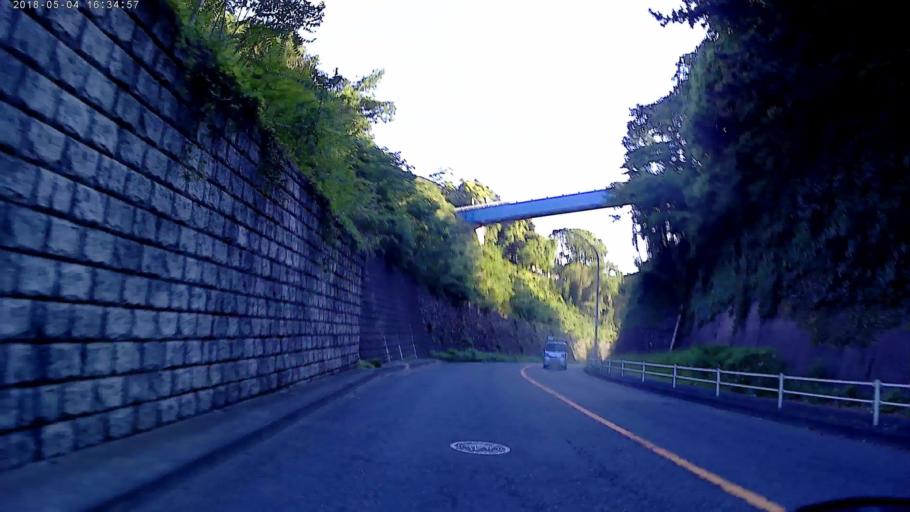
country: JP
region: Kanagawa
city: Yokohama
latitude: 35.4681
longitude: 139.5924
